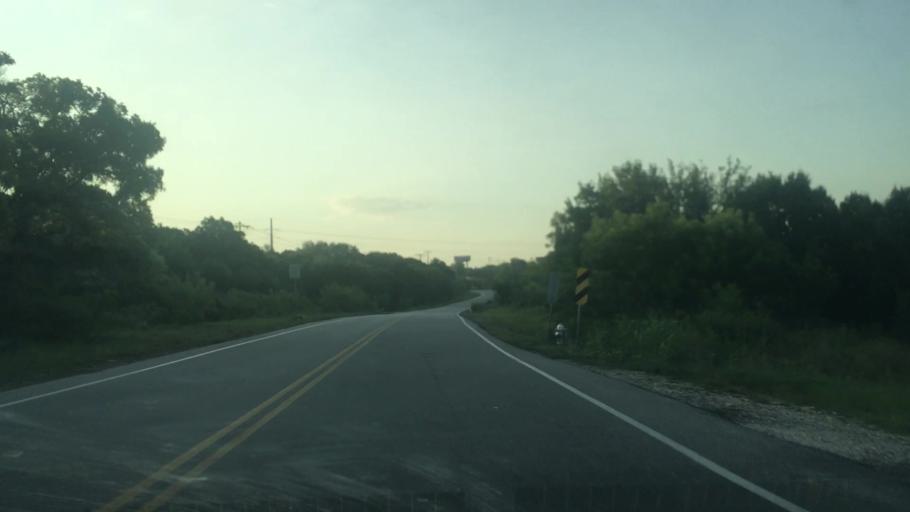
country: US
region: Texas
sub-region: Travis County
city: Hudson Bend
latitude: 30.4073
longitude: -97.8599
